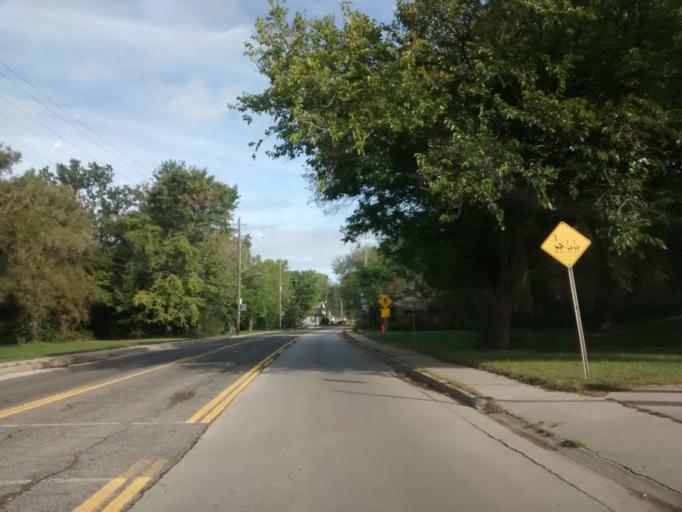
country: CA
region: Ontario
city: Hamilton
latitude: 43.3037
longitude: -79.7989
